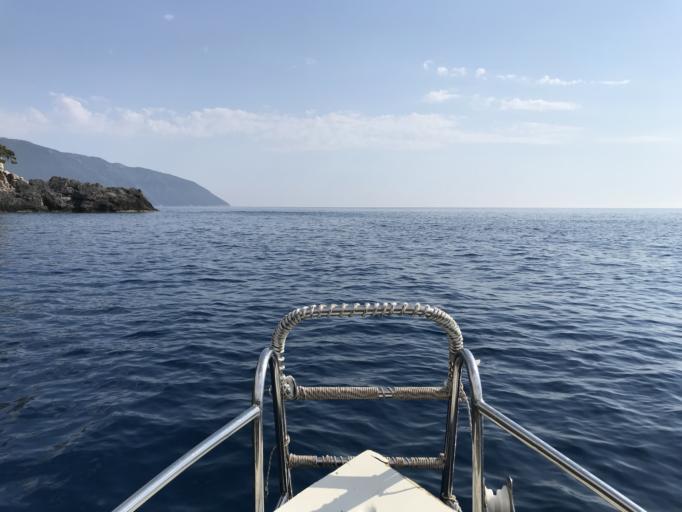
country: TR
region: Mugla
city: OEluedeniz
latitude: 36.4563
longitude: 29.1205
